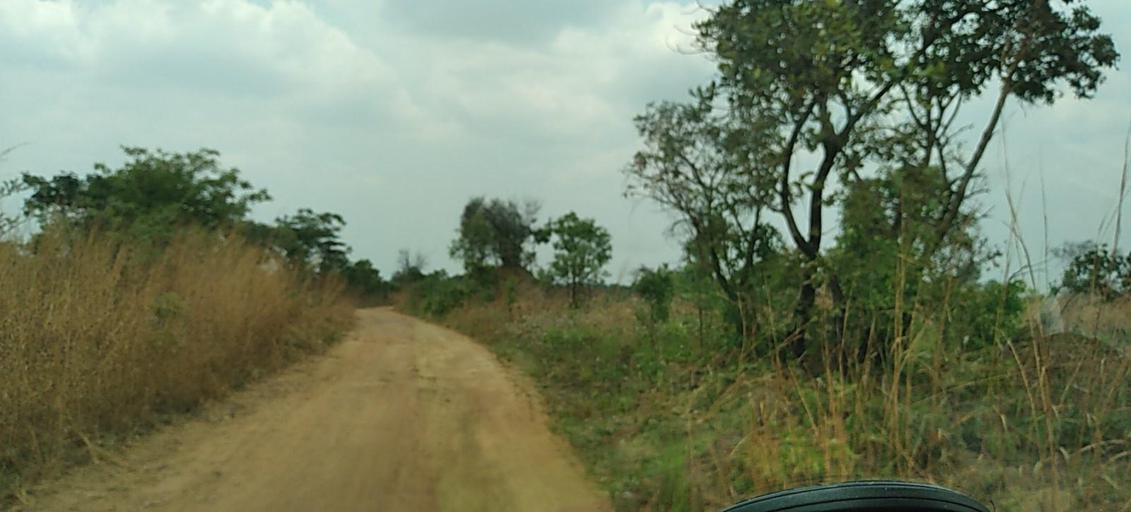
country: ZM
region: North-Western
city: Kansanshi
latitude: -12.0856
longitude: 26.3663
